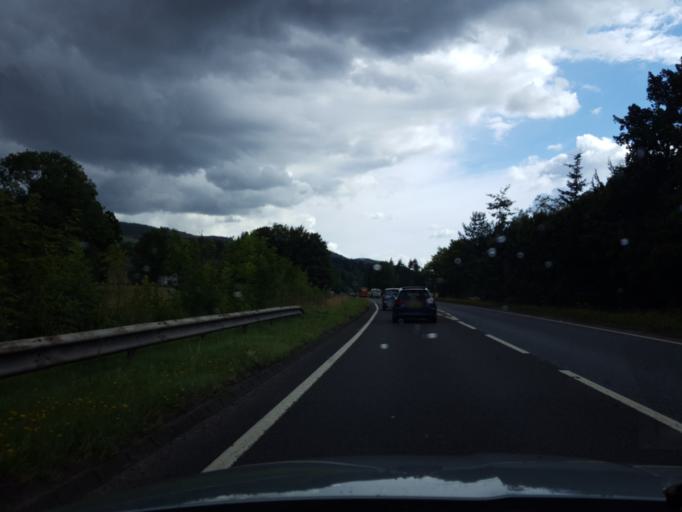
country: GB
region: Scotland
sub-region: Perth and Kinross
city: Pitlochry
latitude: 56.6148
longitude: -3.6303
